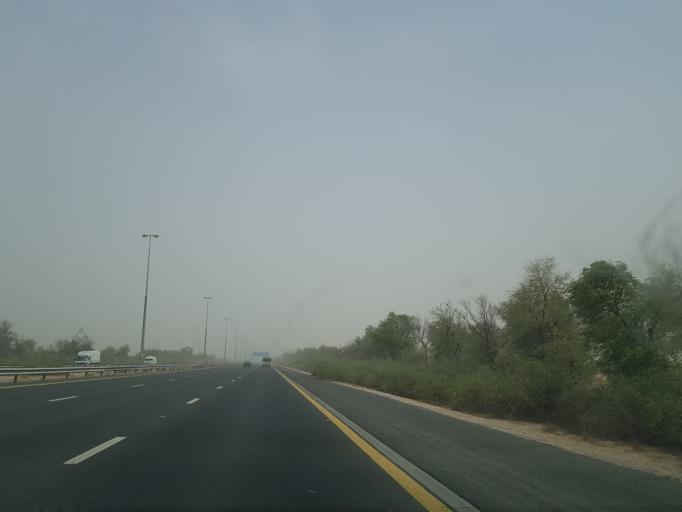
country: AE
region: Dubai
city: Dubai
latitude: 24.9363
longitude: 55.5139
